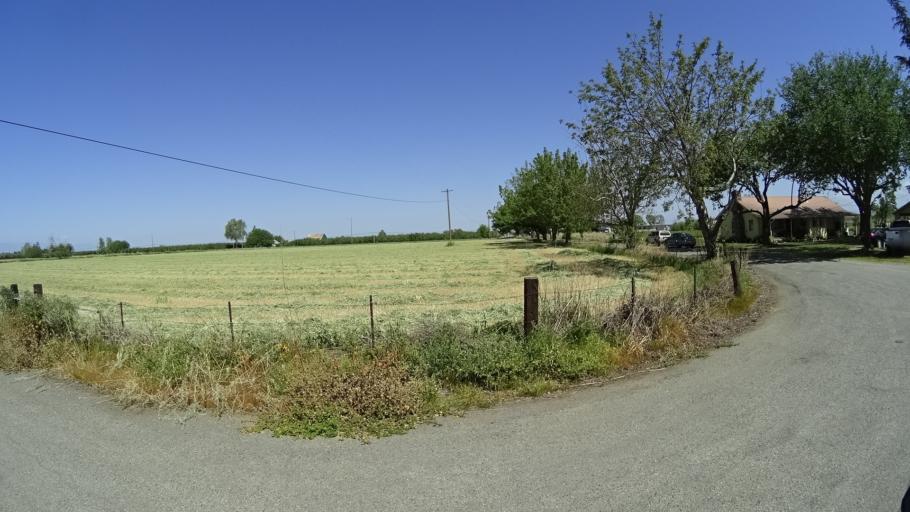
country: US
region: California
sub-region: Glenn County
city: Orland
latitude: 39.7665
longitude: -122.1597
